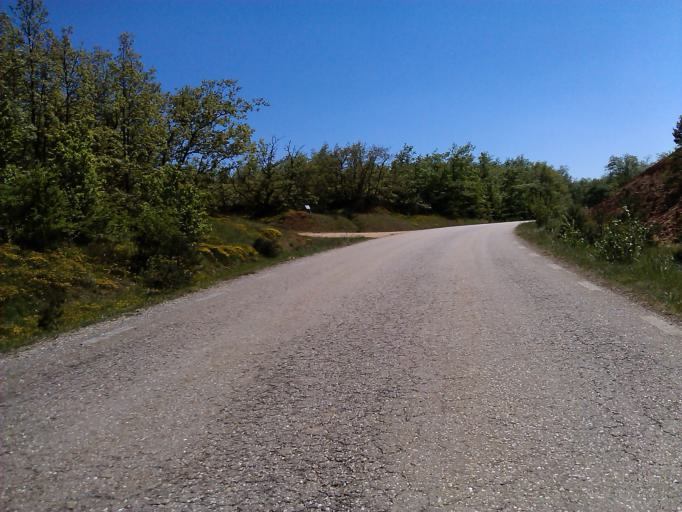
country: ES
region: Castille and Leon
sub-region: Provincia de Burgos
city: Barrios de Colina
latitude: 42.3709
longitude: -3.4424
